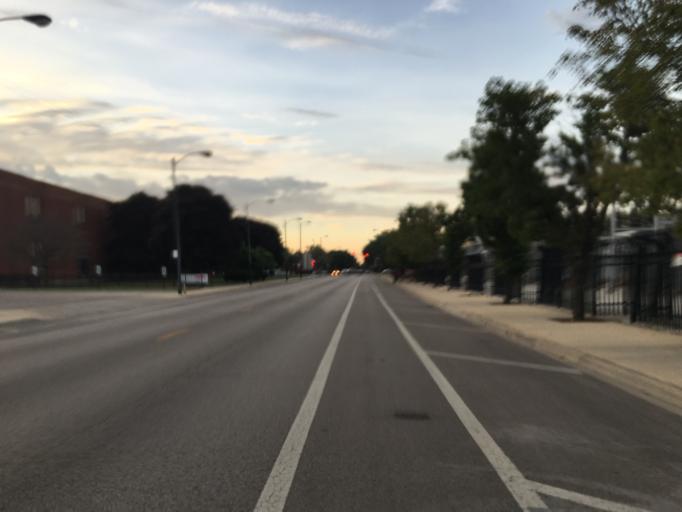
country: US
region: Illinois
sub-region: Cook County
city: Lincolnwood
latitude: 41.9452
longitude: -87.6980
